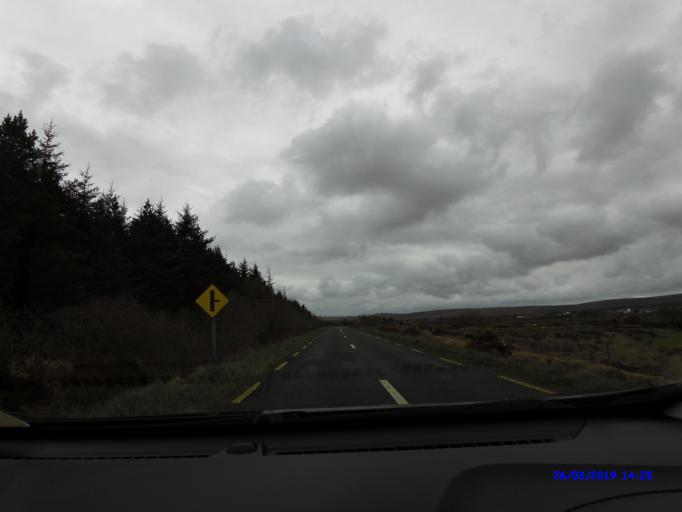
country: IE
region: Connaught
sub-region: Maigh Eo
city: Belmullet
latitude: 54.2407
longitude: -9.6601
